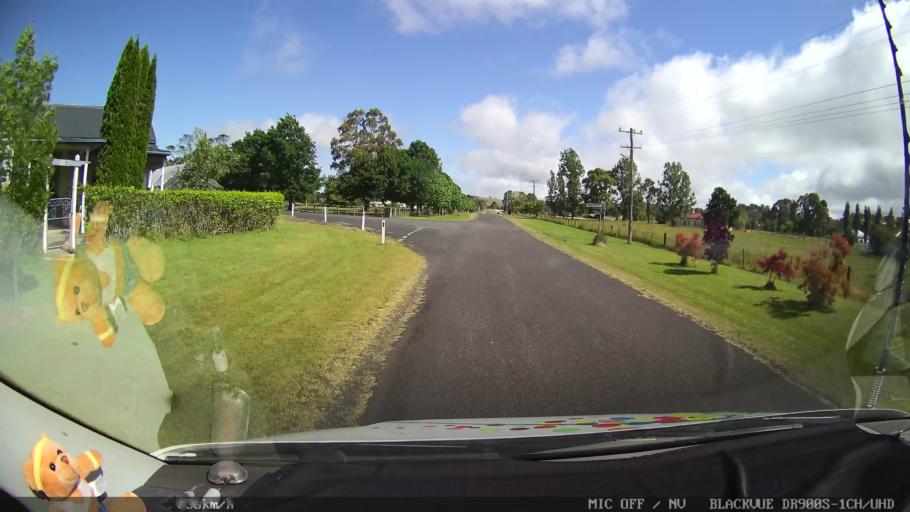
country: AU
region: New South Wales
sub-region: Guyra
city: Guyra
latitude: -30.0230
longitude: 151.6599
